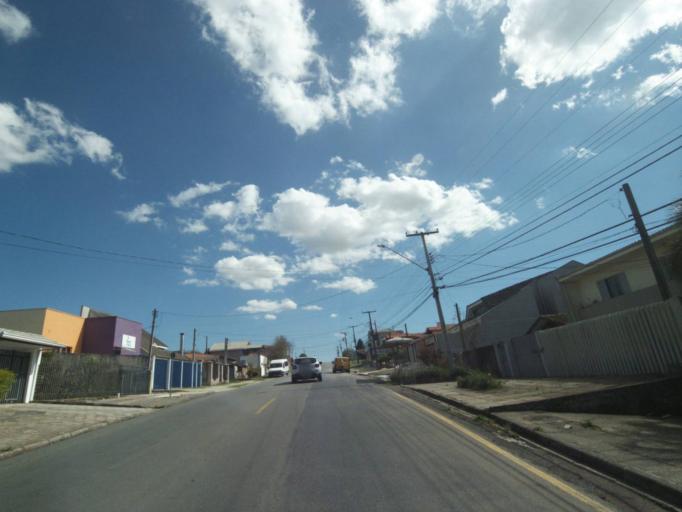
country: BR
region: Parana
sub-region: Curitiba
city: Curitiba
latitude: -25.3808
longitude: -49.2565
